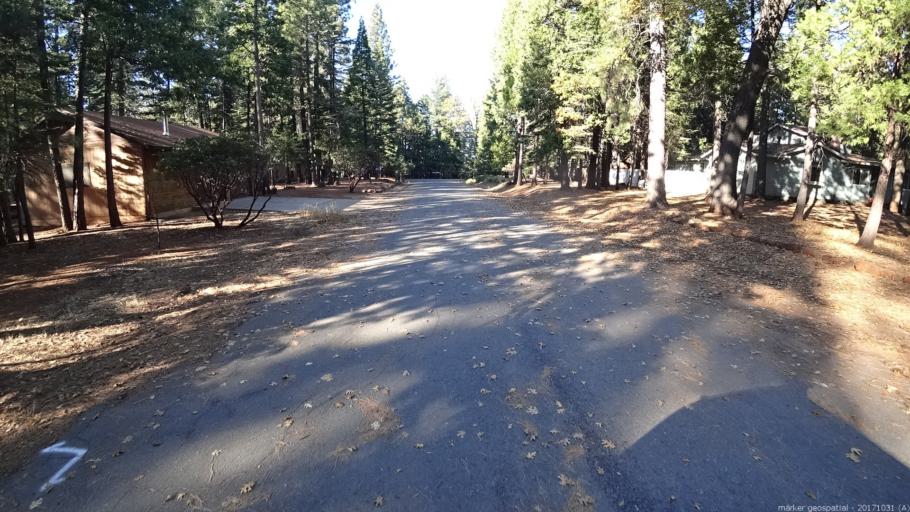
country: US
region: California
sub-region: Shasta County
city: Shingletown
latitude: 40.5032
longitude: -121.9009
